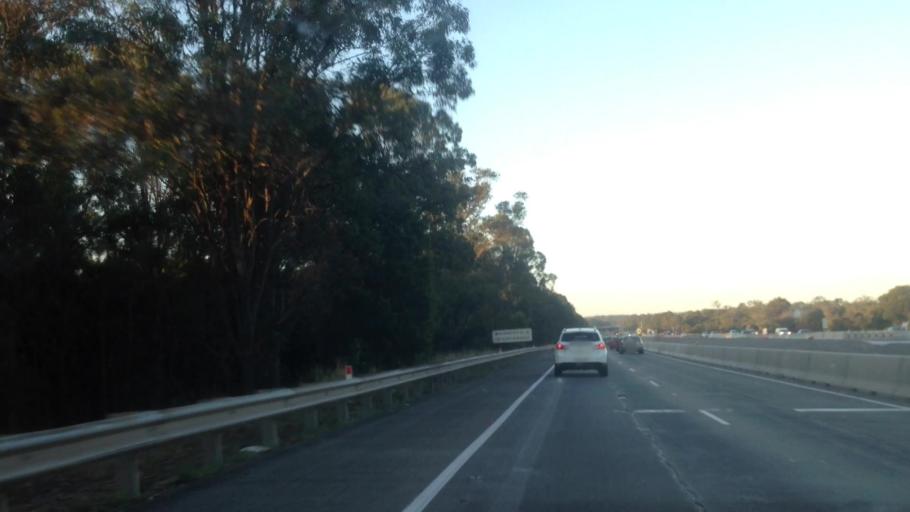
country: AU
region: New South Wales
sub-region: Wyong Shire
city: Jilliby
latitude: -33.2405
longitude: 151.4113
